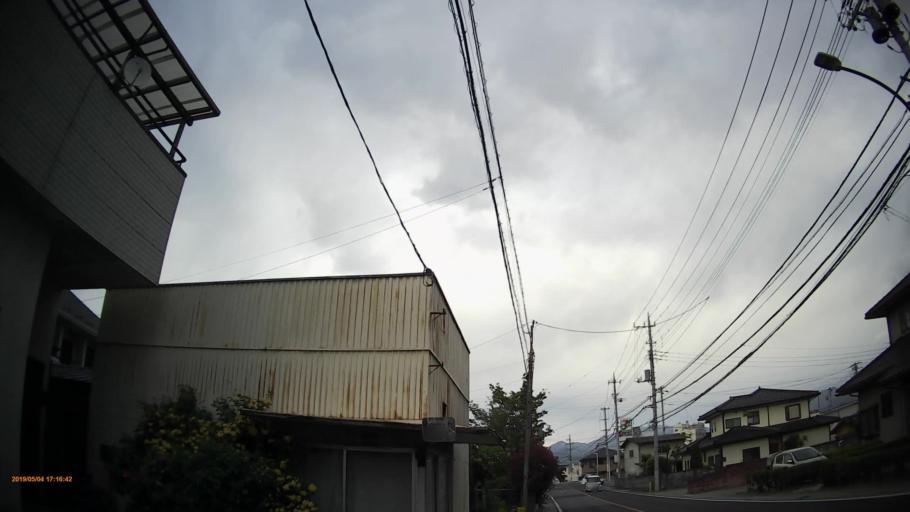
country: JP
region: Yamanashi
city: Isawa
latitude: 35.6518
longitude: 138.6291
